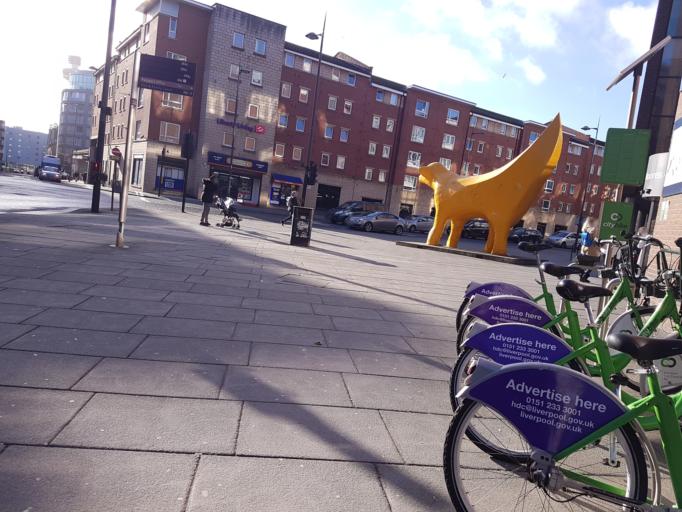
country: GB
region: England
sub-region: Liverpool
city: Liverpool
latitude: 53.4112
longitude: -2.9882
